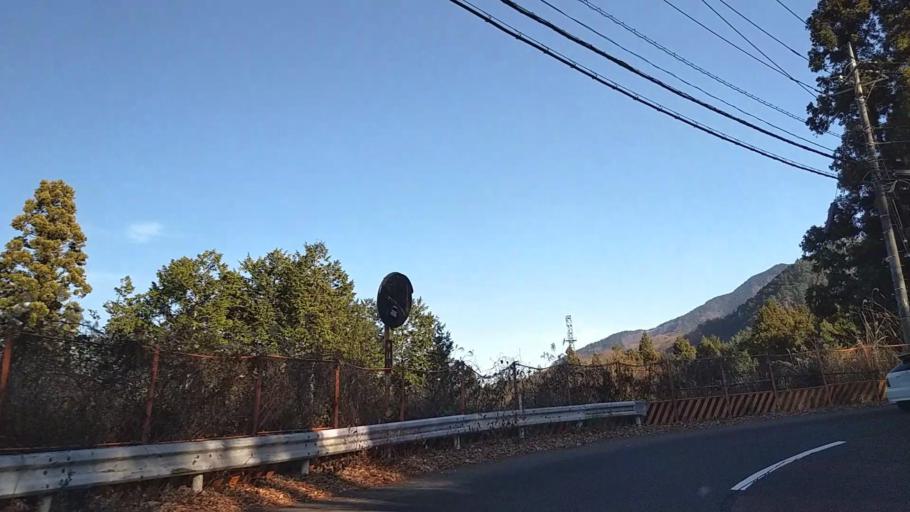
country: JP
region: Yamanashi
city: Uenohara
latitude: 35.5453
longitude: 139.1315
